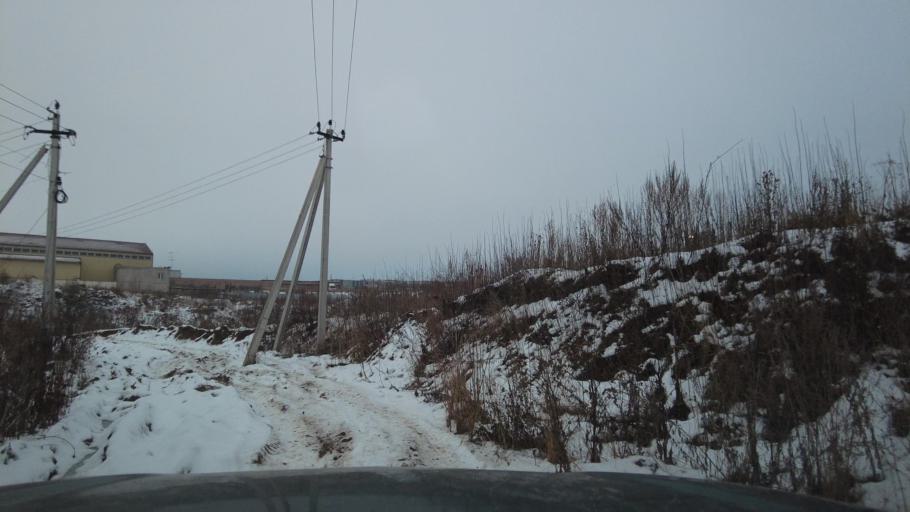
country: RU
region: Moskovskaya
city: Novopodrezkovo
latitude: 55.9895
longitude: 37.3933
